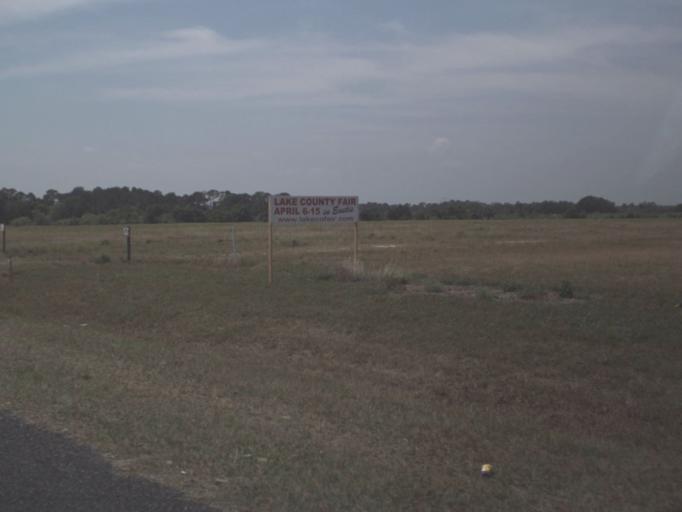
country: US
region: Florida
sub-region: Lake County
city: Eustis
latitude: 28.8876
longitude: -81.6870
